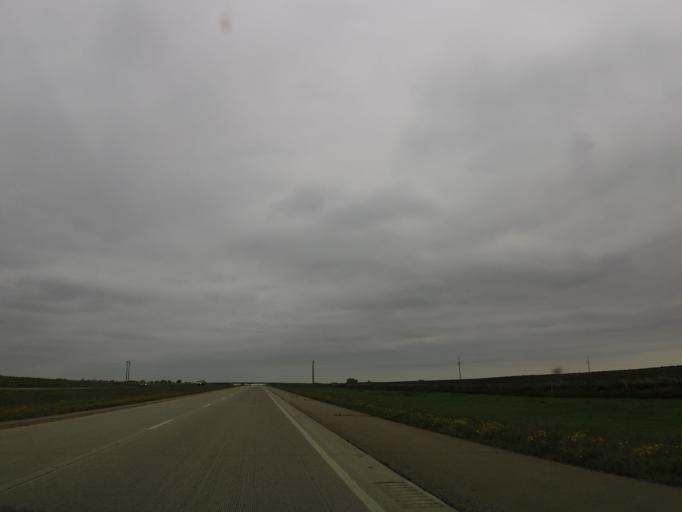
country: US
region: South Dakota
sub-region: Roberts County
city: Sisseton
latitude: 45.4469
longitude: -96.9891
